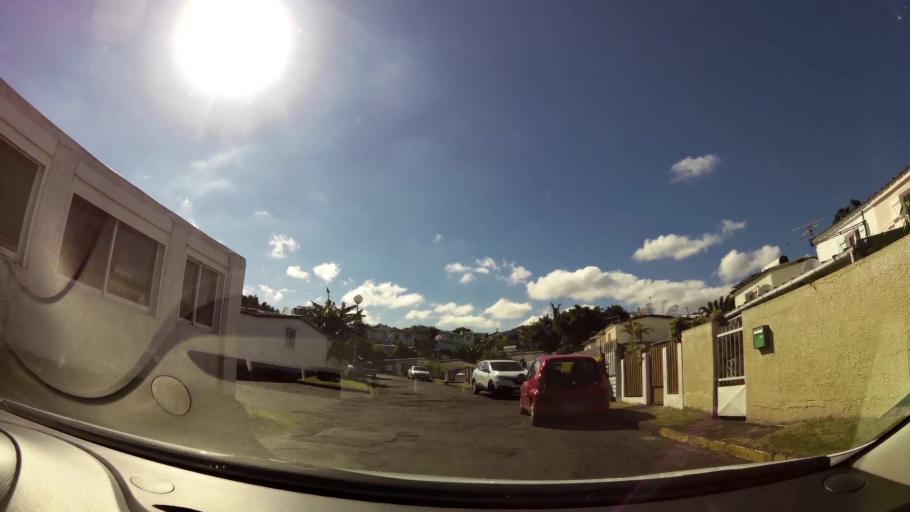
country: RE
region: Reunion
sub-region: Reunion
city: Le Tampon
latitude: -21.2705
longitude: 55.5148
